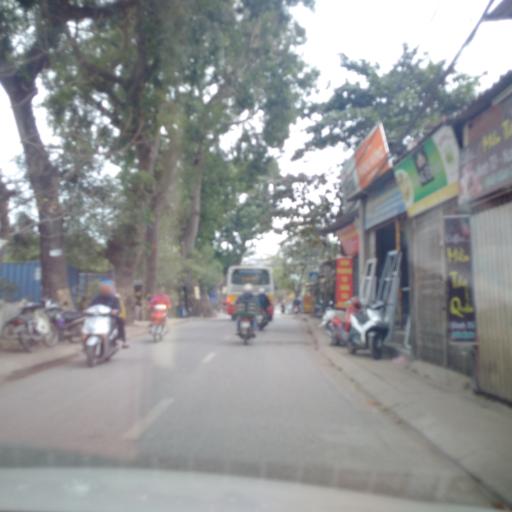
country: VN
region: Ha Noi
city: Tay Ho
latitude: 21.0819
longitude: 105.7781
